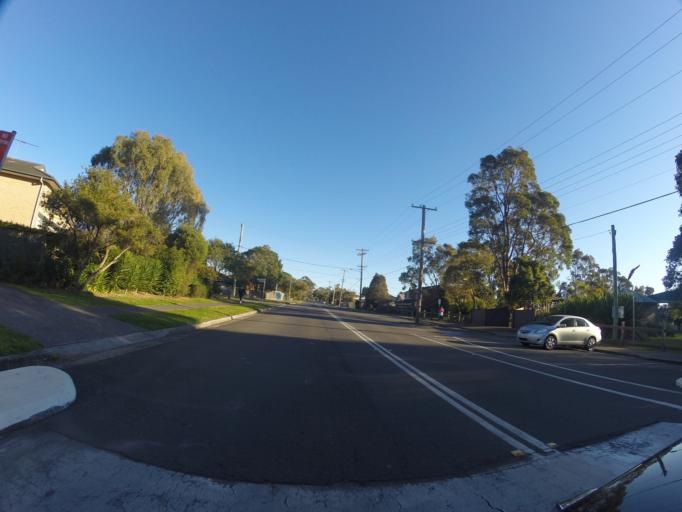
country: AU
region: New South Wales
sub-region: Sutherland Shire
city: Gymea Bay
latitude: -34.0488
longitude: 151.0869
